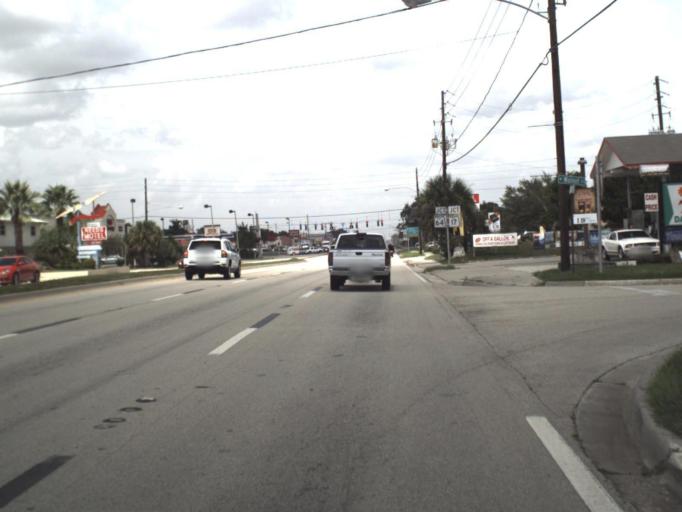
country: US
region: Florida
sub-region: Highlands County
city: Avon Park
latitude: 27.5936
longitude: -81.5143
